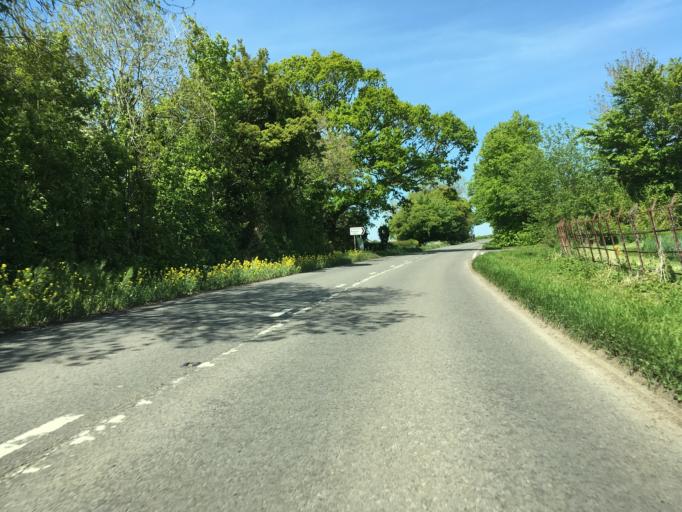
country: GB
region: England
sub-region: Wiltshire
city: Hankerton
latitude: 51.6463
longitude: -2.0594
